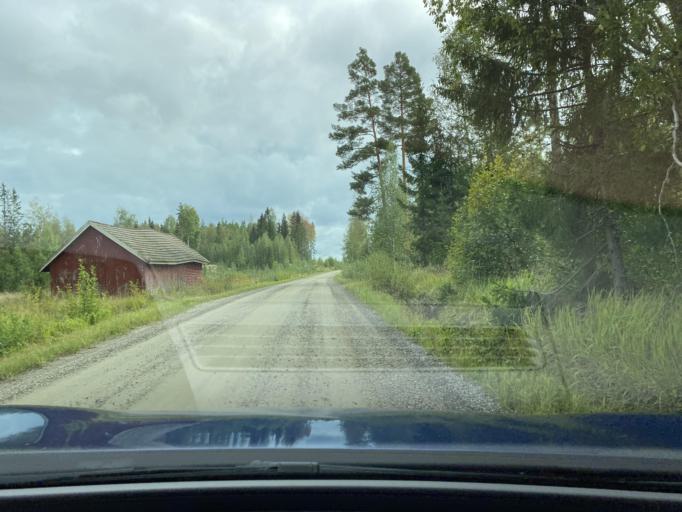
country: FI
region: Pirkanmaa
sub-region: Lounais-Pirkanmaa
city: Punkalaidun
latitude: 61.2320
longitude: 23.1489
